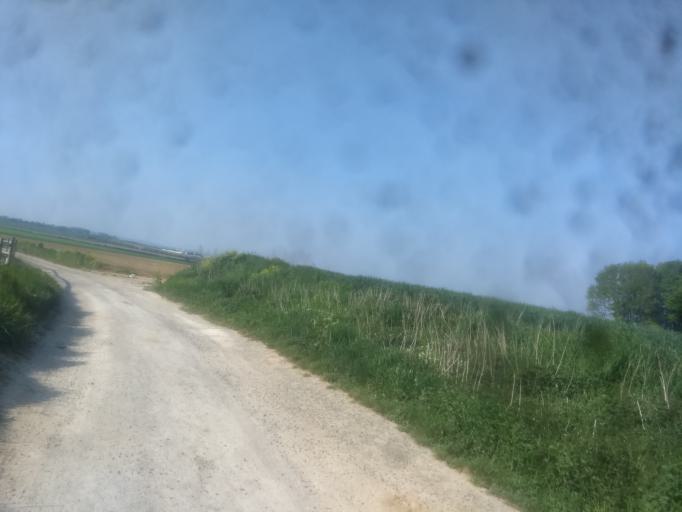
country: FR
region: Nord-Pas-de-Calais
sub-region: Departement du Pas-de-Calais
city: Beaurains
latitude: 50.2649
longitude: 2.8061
